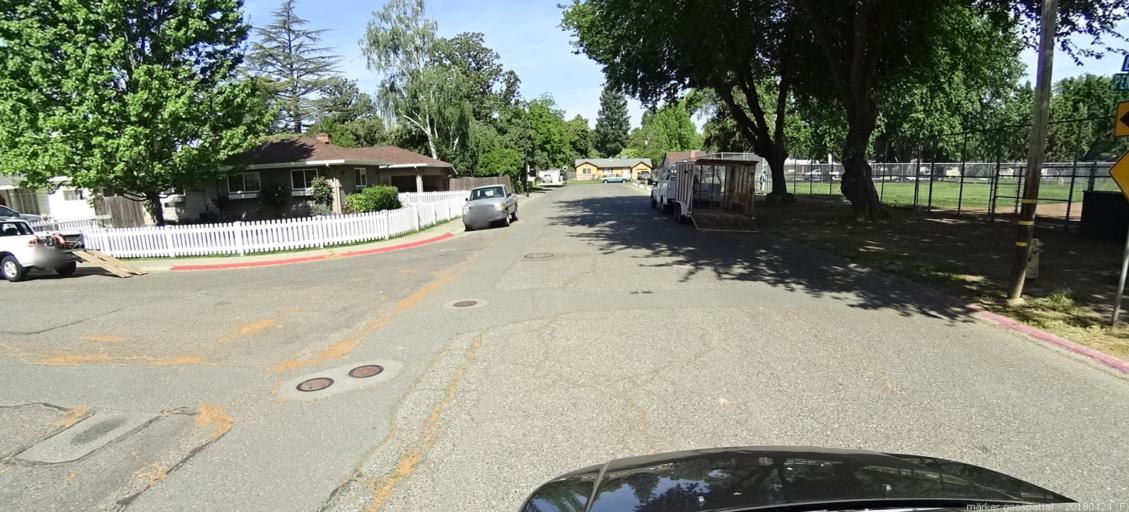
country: US
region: California
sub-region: Yolo County
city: West Sacramento
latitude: 38.5650
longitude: -121.5319
